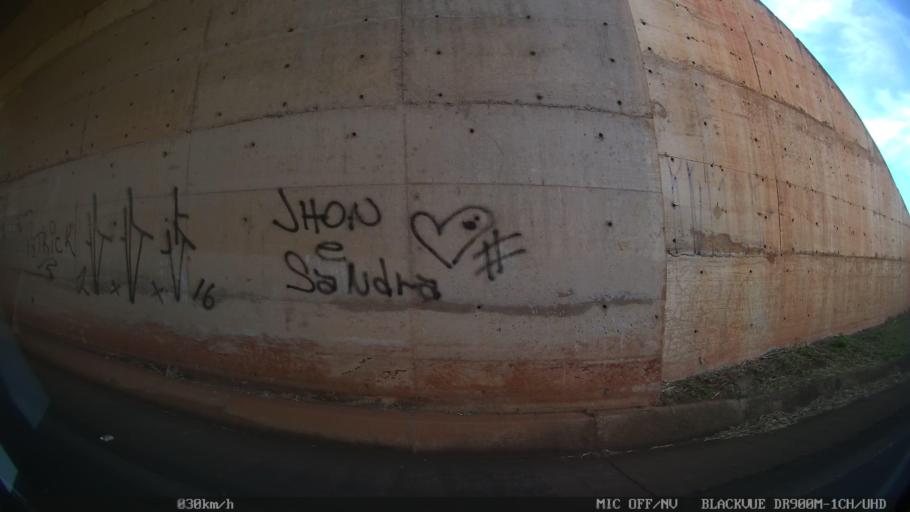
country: BR
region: Sao Paulo
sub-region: Sao Jose Do Rio Preto
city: Sao Jose do Rio Preto
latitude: -20.7348
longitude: -49.3375
